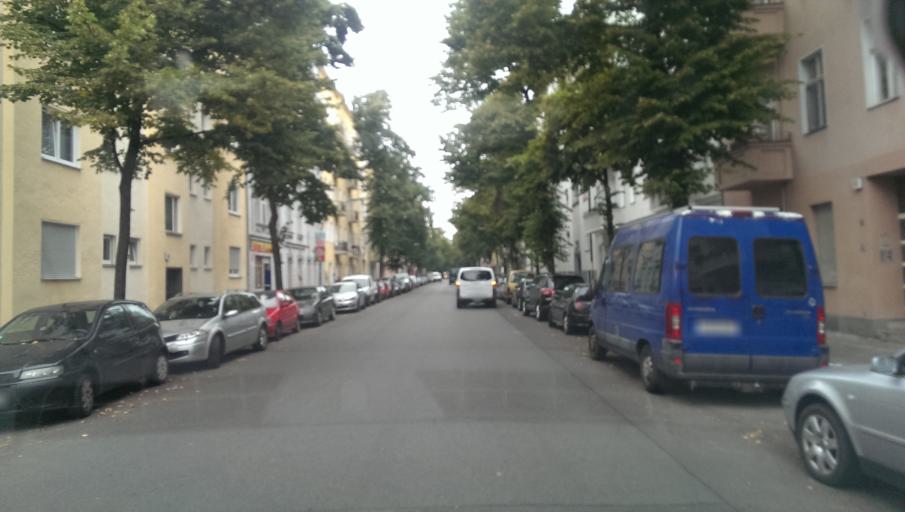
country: DE
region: Berlin
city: Britz
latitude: 52.4682
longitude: 13.4277
